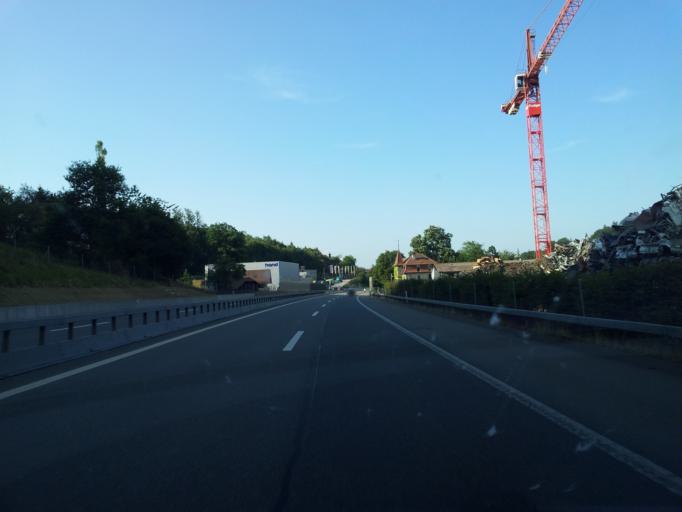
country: CH
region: Fribourg
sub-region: Sense District
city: Flamatt
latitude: 46.9039
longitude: 7.3554
